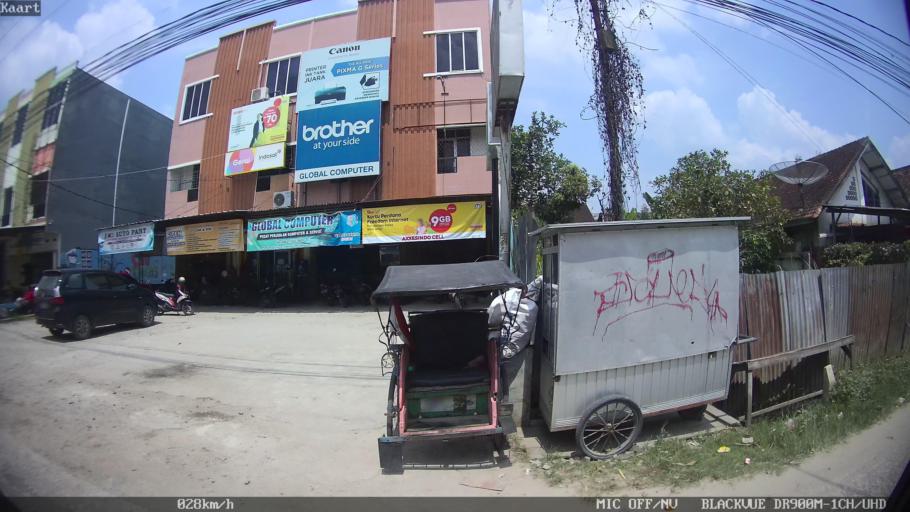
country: ID
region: Lampung
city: Pringsewu
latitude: -5.3524
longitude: 104.9763
